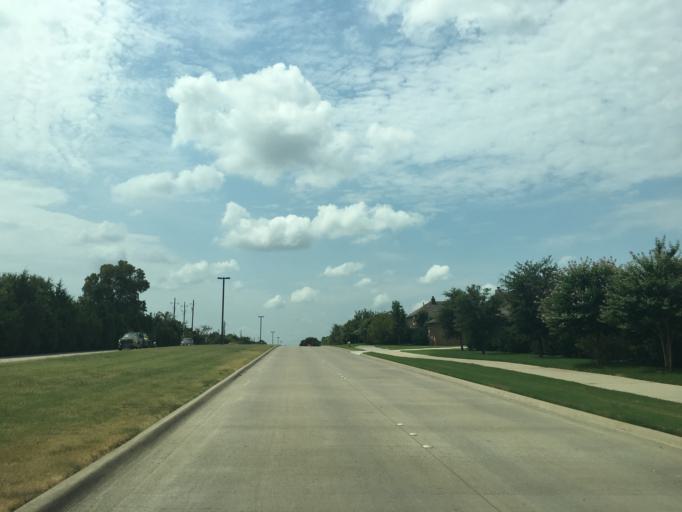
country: US
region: Texas
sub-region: Rockwall County
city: Rockwall
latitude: 32.9481
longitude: -96.4424
